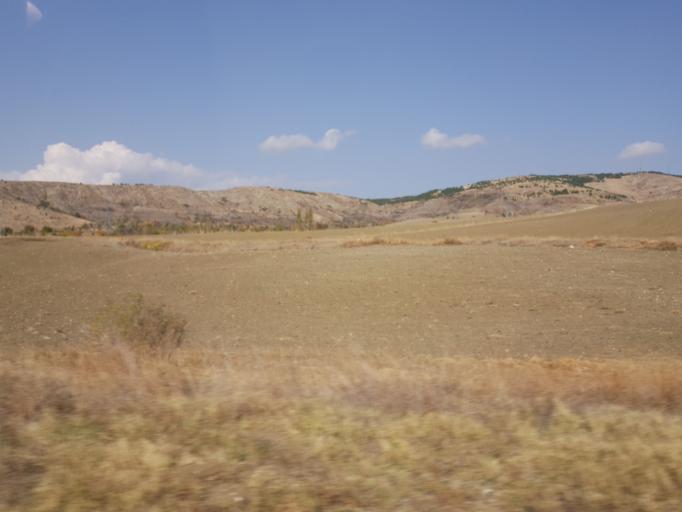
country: TR
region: Corum
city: Bogazkale
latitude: 40.1583
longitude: 34.6205
